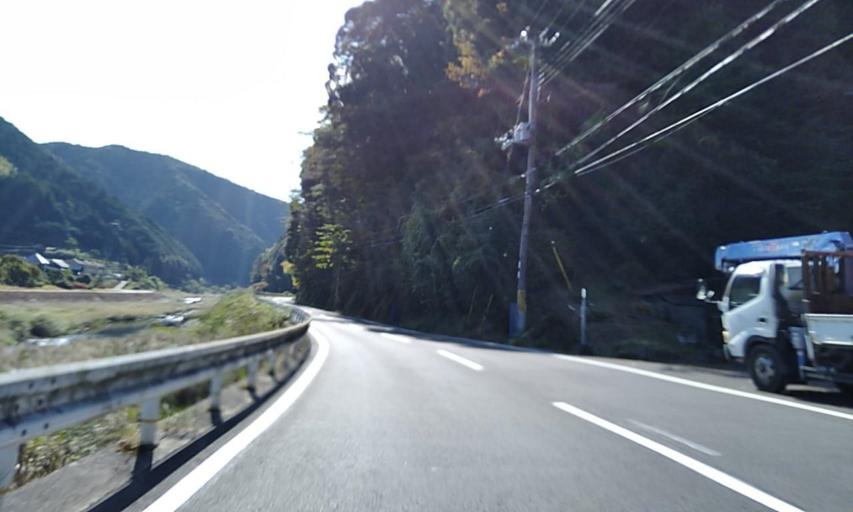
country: JP
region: Wakayama
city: Kainan
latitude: 34.0692
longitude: 135.3550
